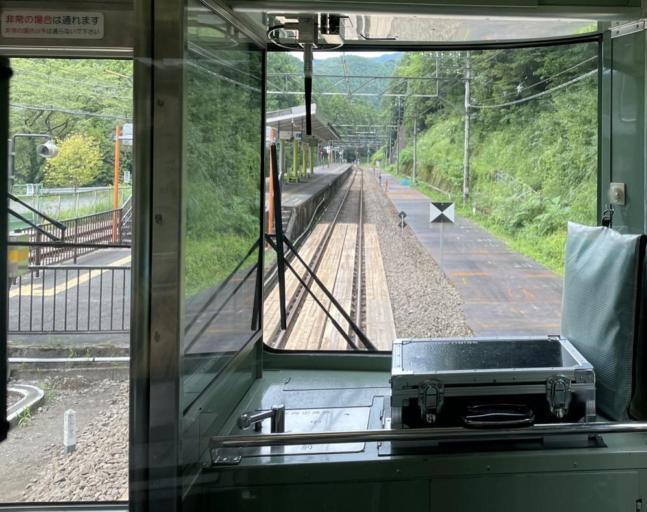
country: JP
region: Saitama
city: Morohongo
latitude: 35.9264
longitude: 139.2025
